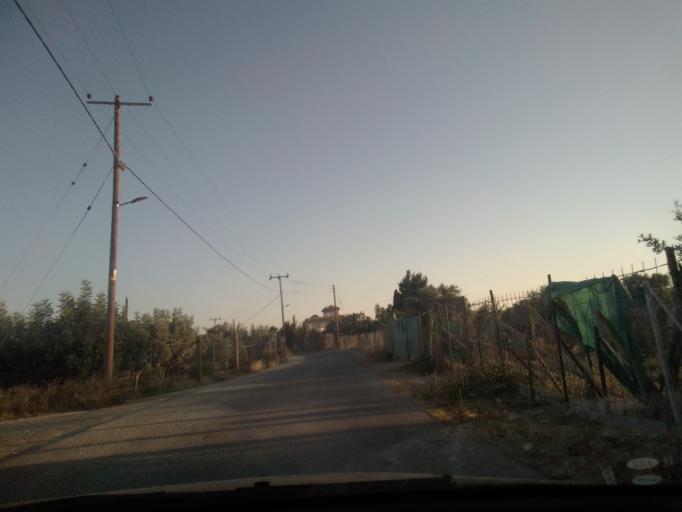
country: CY
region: Limassol
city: Ypsonas
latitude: 34.6757
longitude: 32.9625
